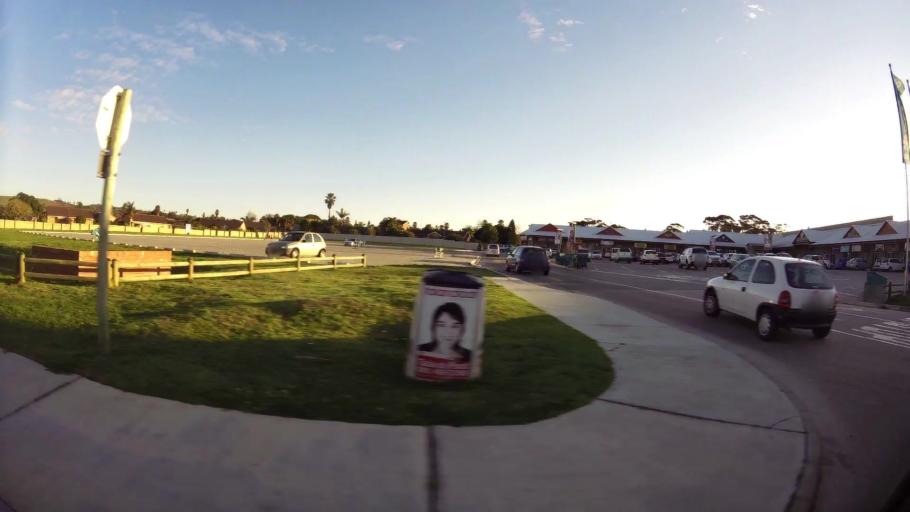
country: ZA
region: Eastern Cape
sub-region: Nelson Mandela Bay Metropolitan Municipality
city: Port Elizabeth
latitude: -33.9700
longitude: 25.4947
